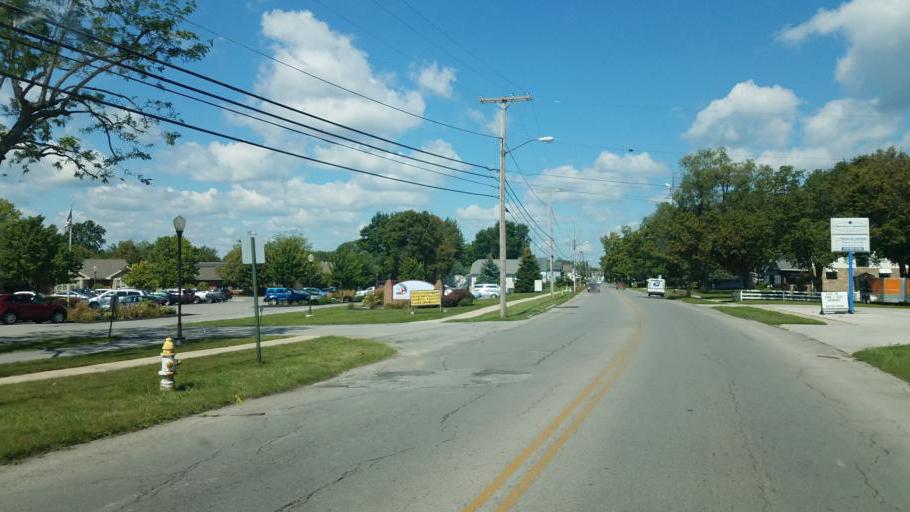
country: US
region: Ohio
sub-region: Seneca County
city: Fostoria
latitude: 41.1476
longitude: -83.3983
